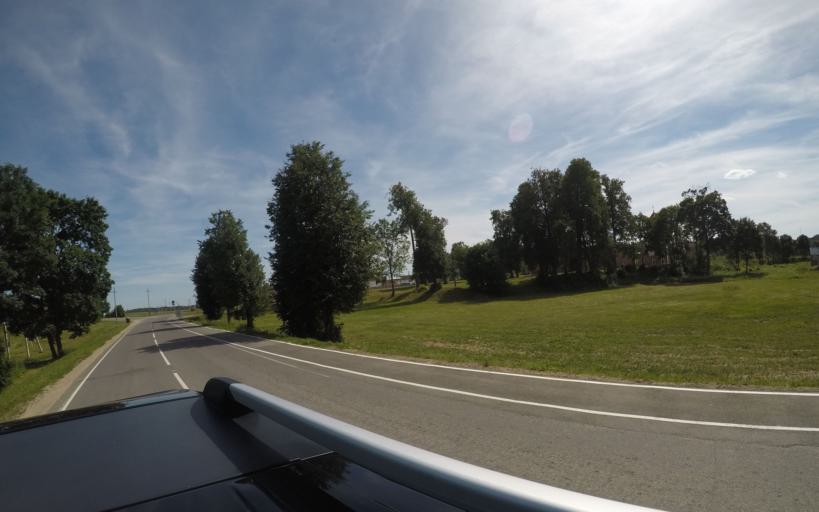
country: BY
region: Grodnenskaya
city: Hal'shany
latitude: 54.2526
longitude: 26.0217
